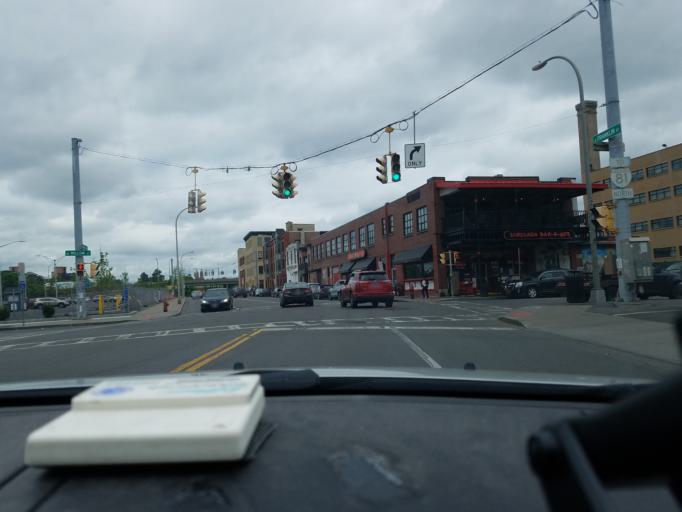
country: US
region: New York
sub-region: Onondaga County
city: Syracuse
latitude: 43.0521
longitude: -76.1548
